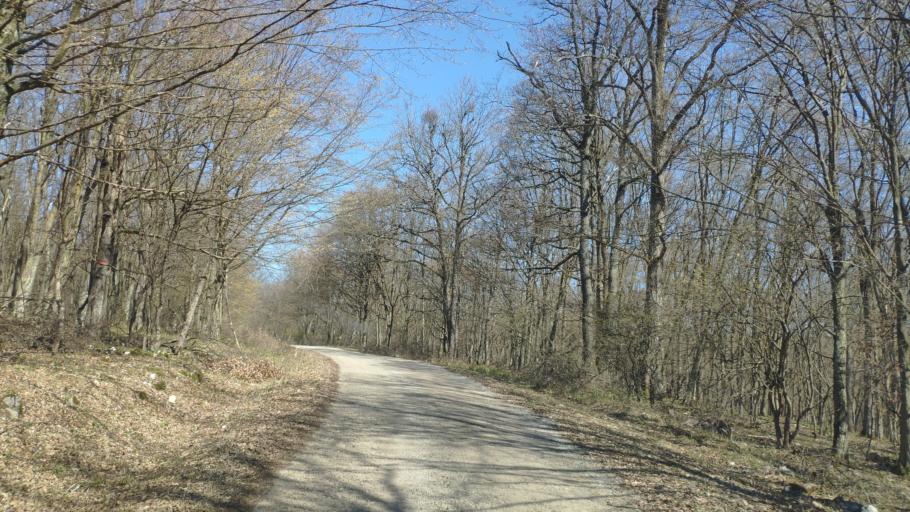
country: SK
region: Kosicky
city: Roznava
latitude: 48.5926
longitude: 20.4094
